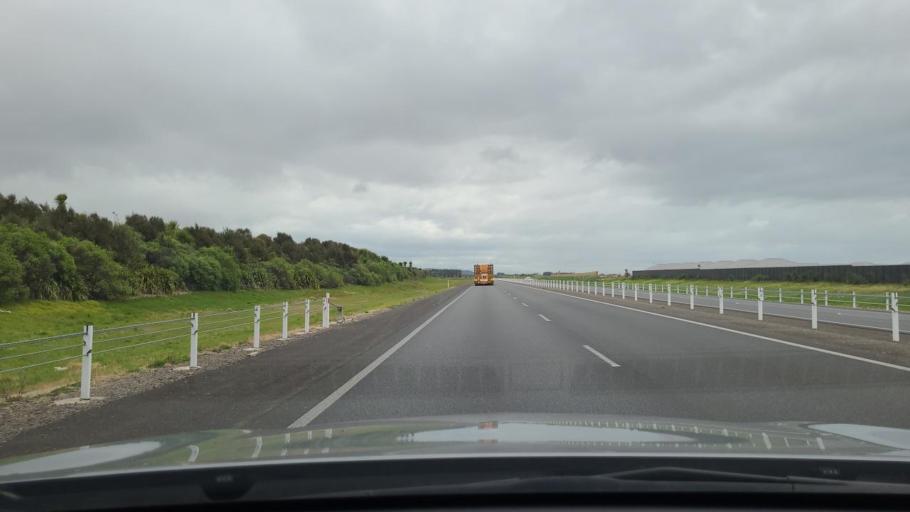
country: NZ
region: Bay of Plenty
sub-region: Western Bay of Plenty District
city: Maketu
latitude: -37.7293
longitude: 176.3343
